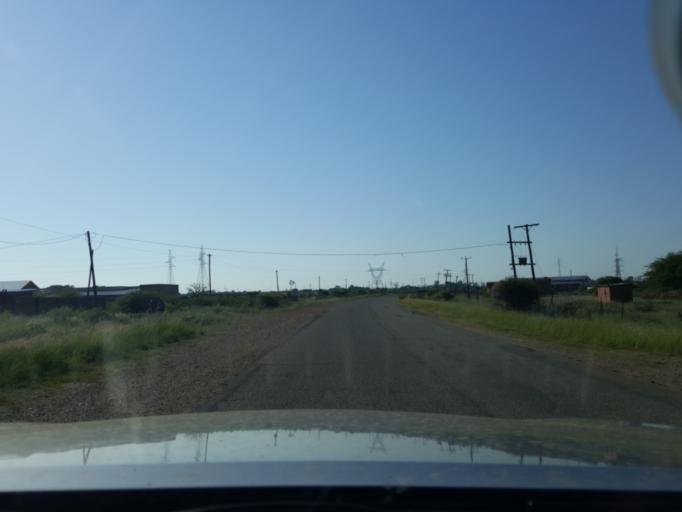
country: ZA
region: North-West
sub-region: Ngaka Modiri Molema District Municipality
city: Mahikeng
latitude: -25.8393
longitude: 25.6729
